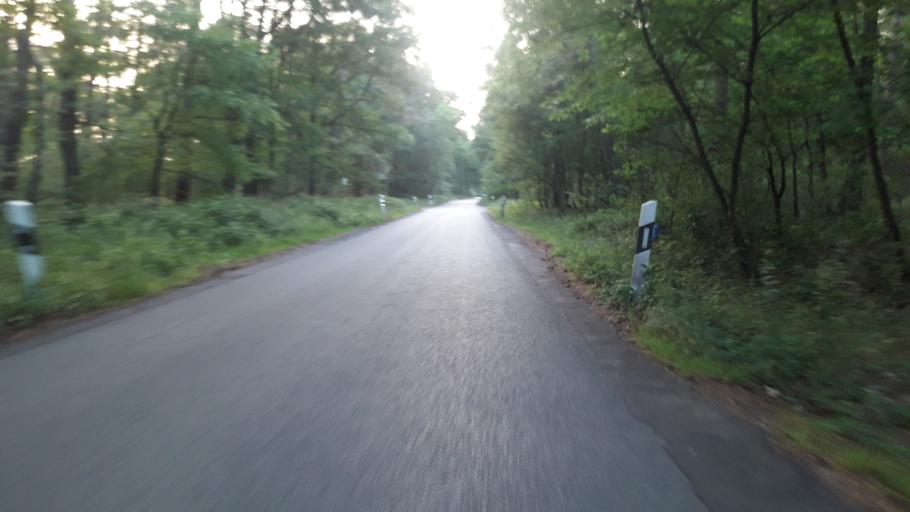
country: DE
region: North Rhine-Westphalia
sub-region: Regierungsbezirk Detmold
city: Hovelhof
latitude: 51.8628
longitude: 8.6552
